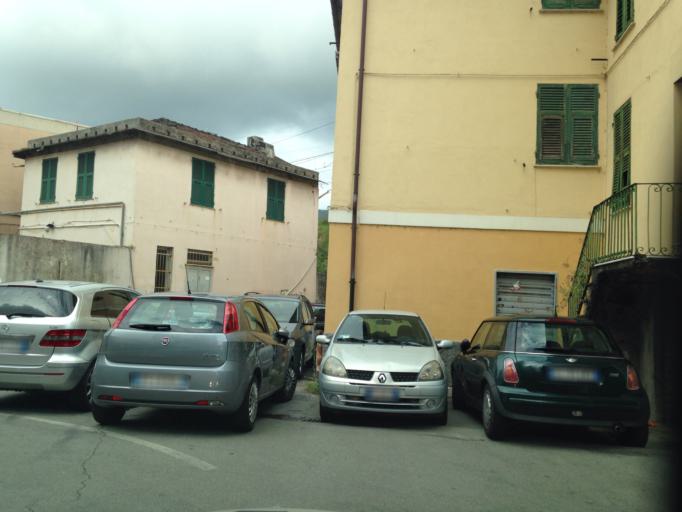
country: IT
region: Liguria
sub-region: Provincia di Genova
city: Genoa
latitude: 44.4571
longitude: 8.8999
